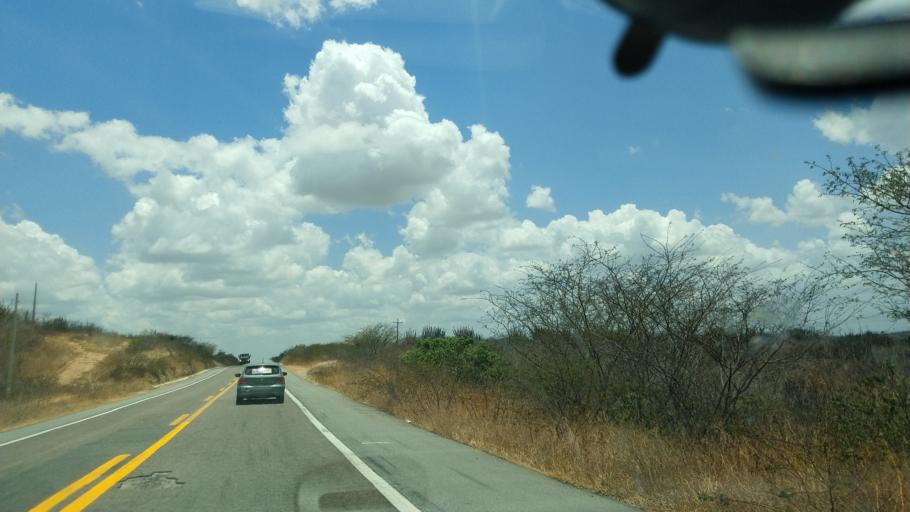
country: BR
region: Rio Grande do Norte
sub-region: Cerro Cora
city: Cerro Cora
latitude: -6.1981
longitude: -36.2683
